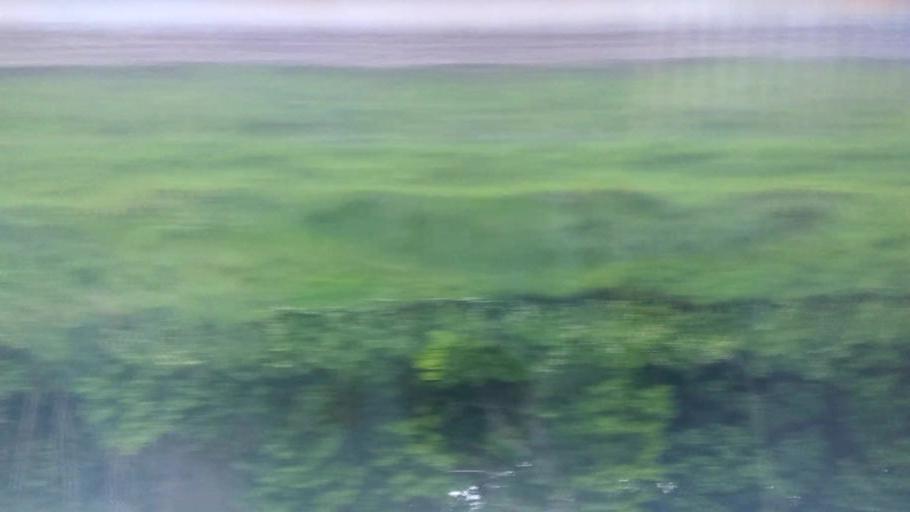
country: RU
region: Moskovskaya
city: Vostryakovo
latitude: 55.3997
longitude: 37.8019
